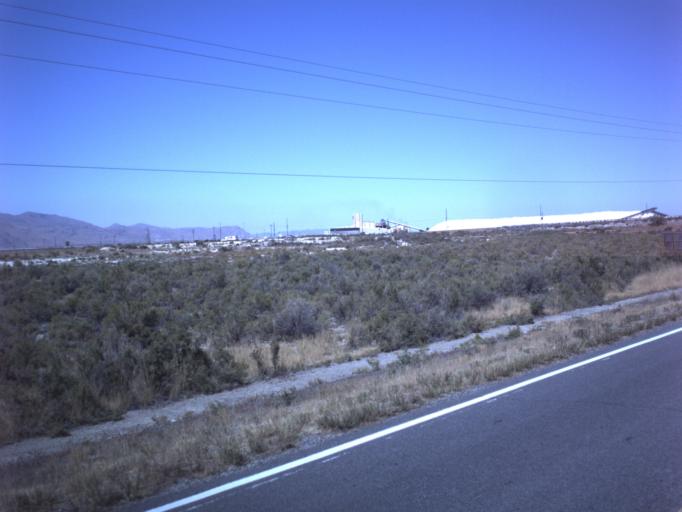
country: US
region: Utah
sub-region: Tooele County
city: Grantsville
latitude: 40.7413
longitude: -112.6542
